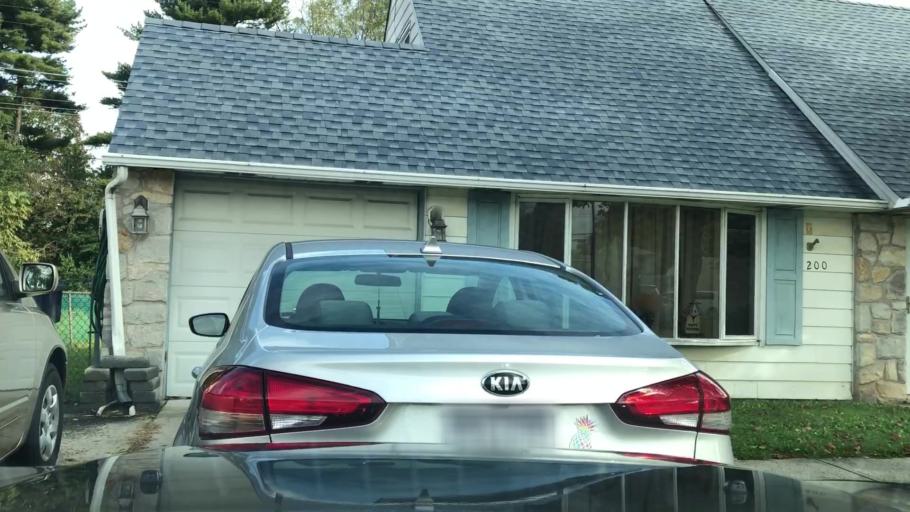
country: US
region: Pennsylvania
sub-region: Bucks County
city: Tullytown
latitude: 40.1404
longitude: -74.8250
